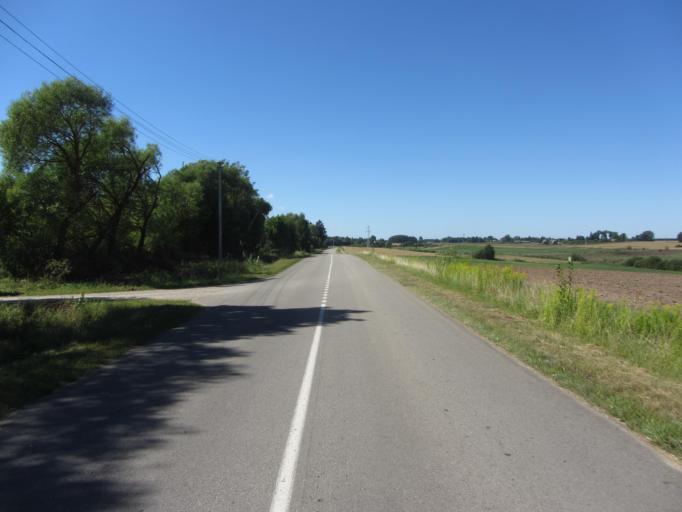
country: LT
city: Kupiskis
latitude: 55.8406
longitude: 25.0432
